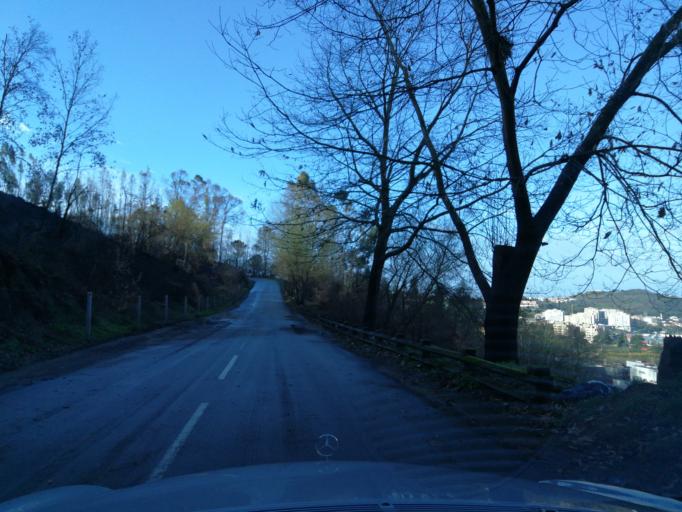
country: PT
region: Braga
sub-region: Braga
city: Braga
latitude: 41.5424
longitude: -8.3888
